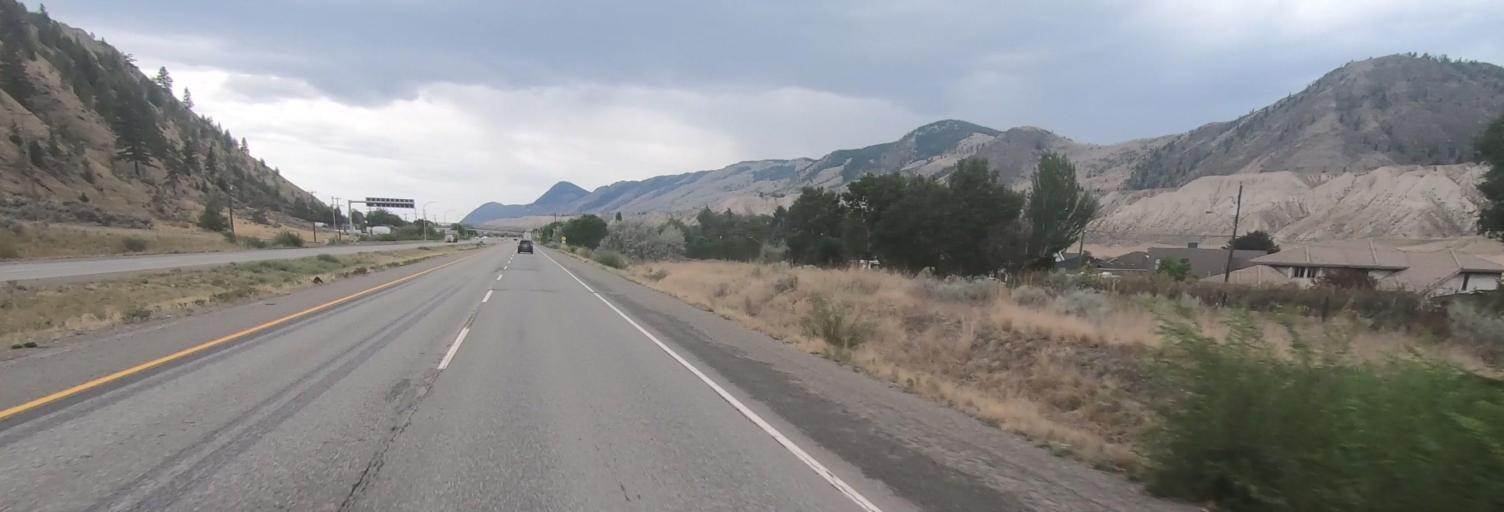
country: CA
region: British Columbia
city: Kamloops
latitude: 50.6646
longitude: -120.1378
